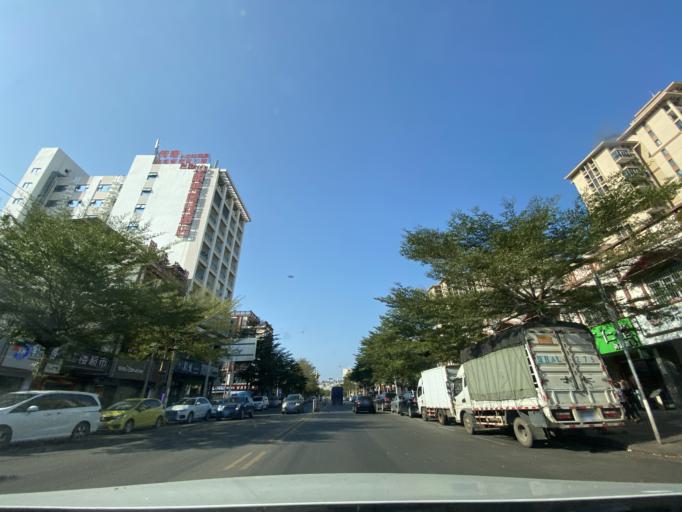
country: CN
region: Hainan
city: Yingzhou
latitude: 18.4247
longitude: 109.8551
